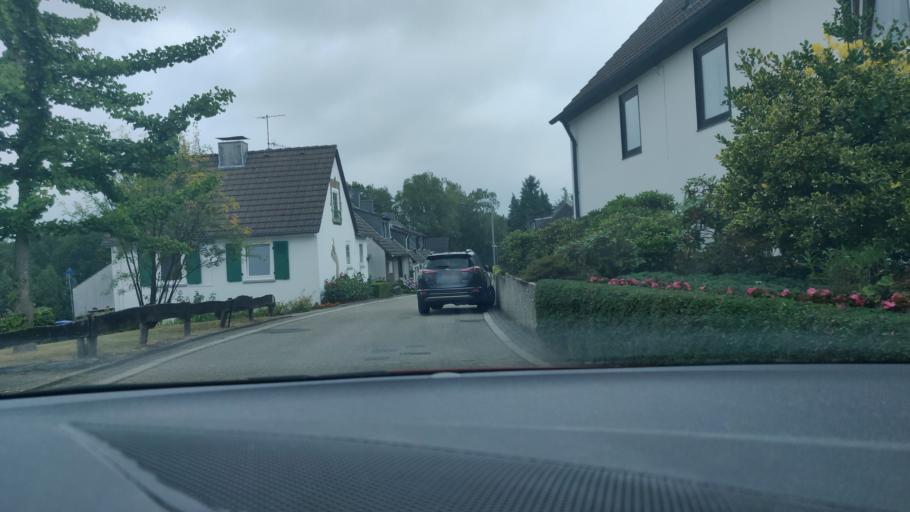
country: DE
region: North Rhine-Westphalia
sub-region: Regierungsbezirk Dusseldorf
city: Velbert
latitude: 51.3531
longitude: 7.0303
